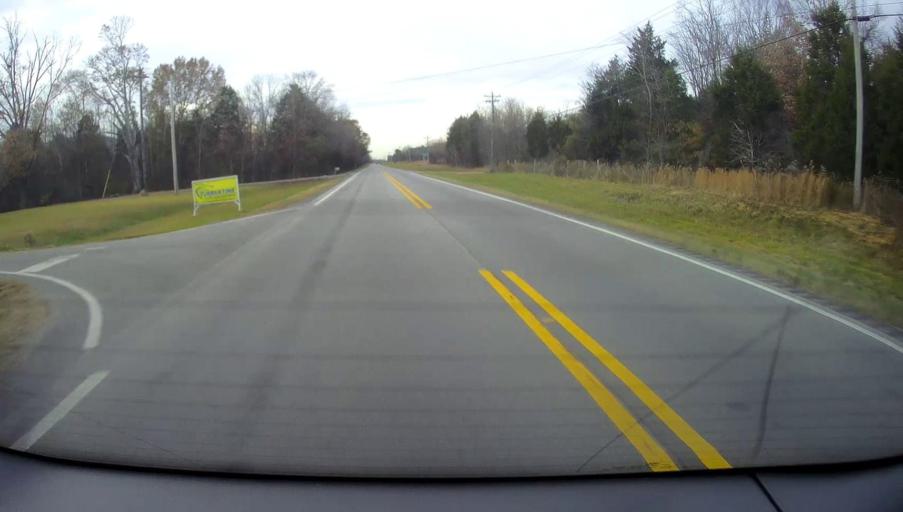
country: US
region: Alabama
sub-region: Morgan County
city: Falkville
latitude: 34.4312
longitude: -86.7317
